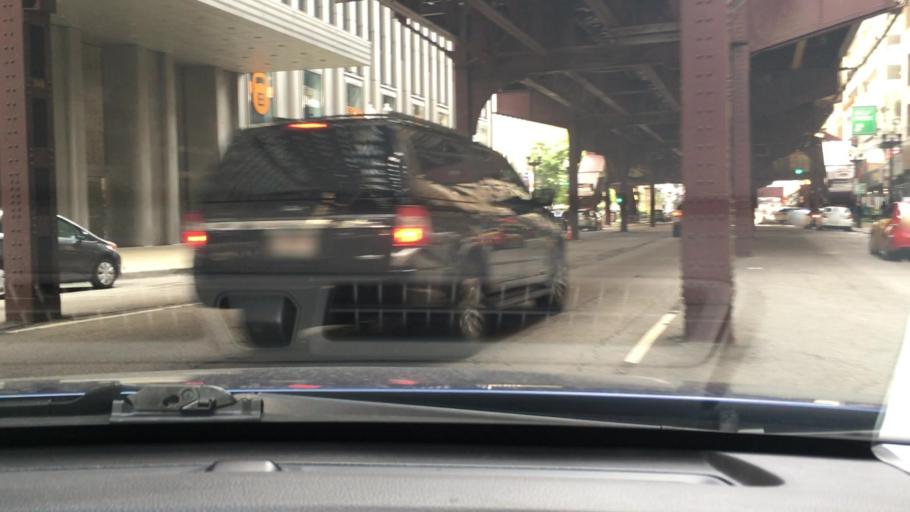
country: US
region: Illinois
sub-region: Cook County
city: Chicago
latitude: 41.8804
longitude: -87.6265
